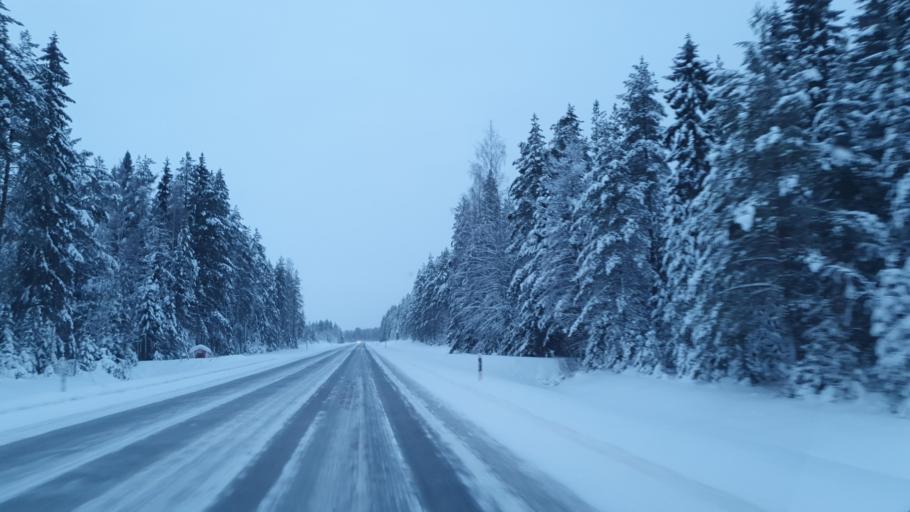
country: FI
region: Kainuu
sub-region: Kajaani
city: Vaala
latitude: 64.6175
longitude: 26.6067
